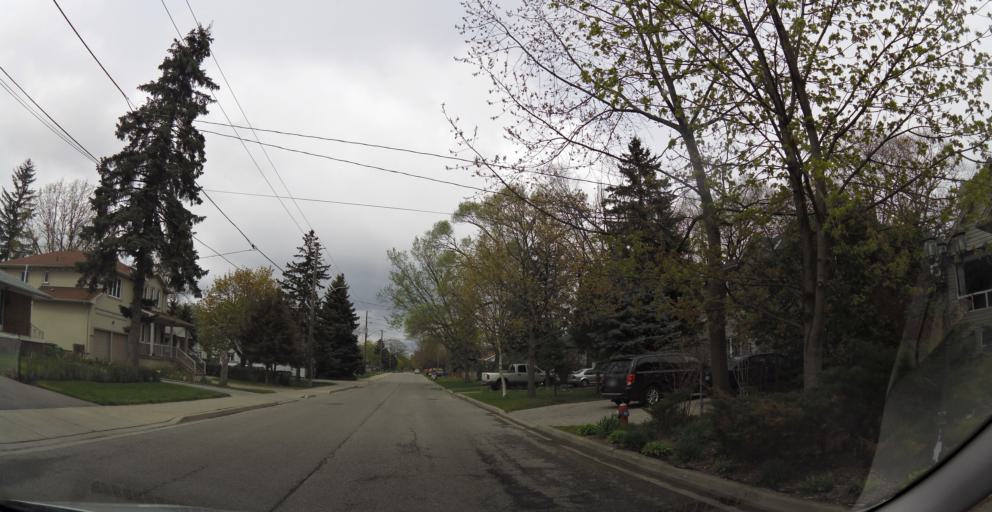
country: CA
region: Ontario
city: Mississauga
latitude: 43.5615
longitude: -79.5835
